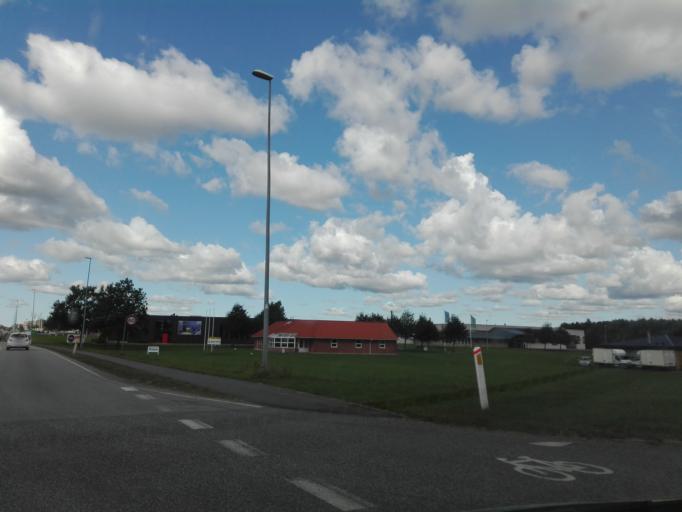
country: DK
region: North Denmark
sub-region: Mariagerfjord Kommune
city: Hobro
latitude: 56.6229
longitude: 9.8063
